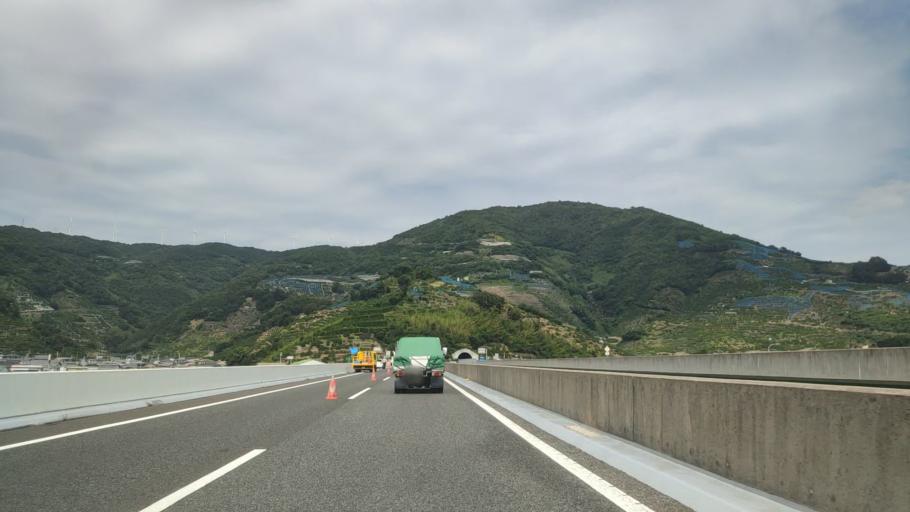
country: JP
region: Wakayama
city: Kainan
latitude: 34.0732
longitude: 135.2006
